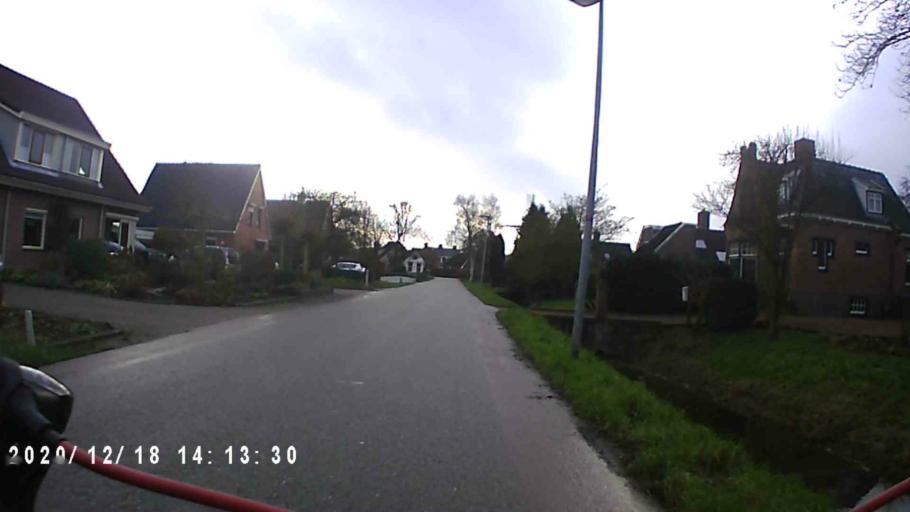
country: NL
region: Groningen
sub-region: Gemeente Bedum
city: Bedum
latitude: 53.2706
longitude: 6.6533
